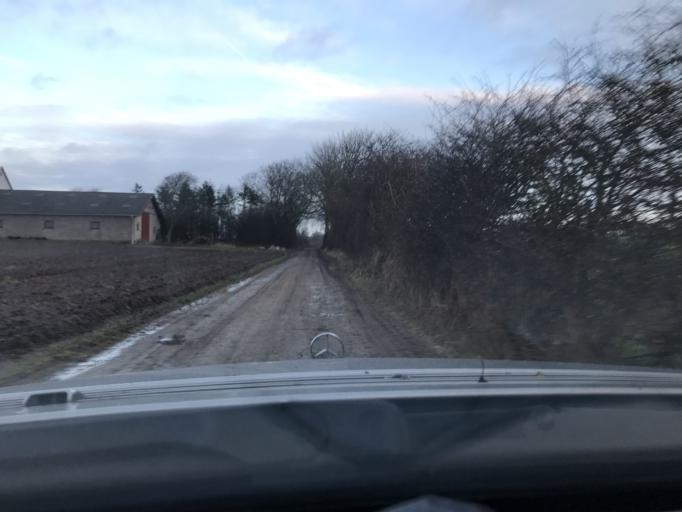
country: DK
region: South Denmark
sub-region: Sonderborg Kommune
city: Nordborg
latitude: 55.0638
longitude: 9.6797
